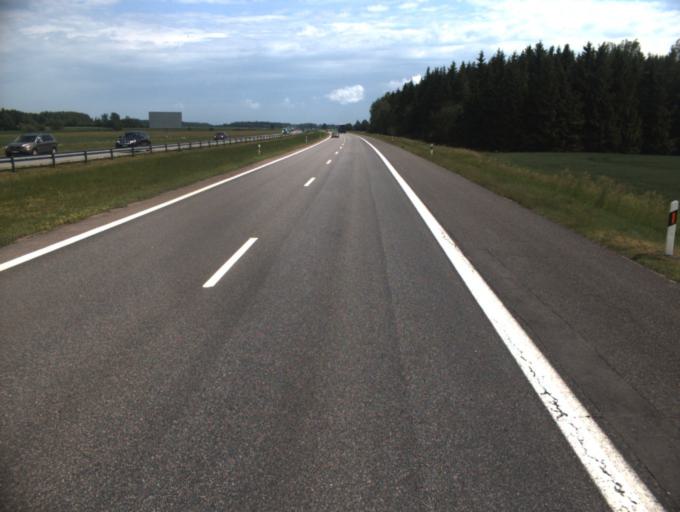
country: LT
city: Ariogala
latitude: 55.2843
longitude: 23.3076
